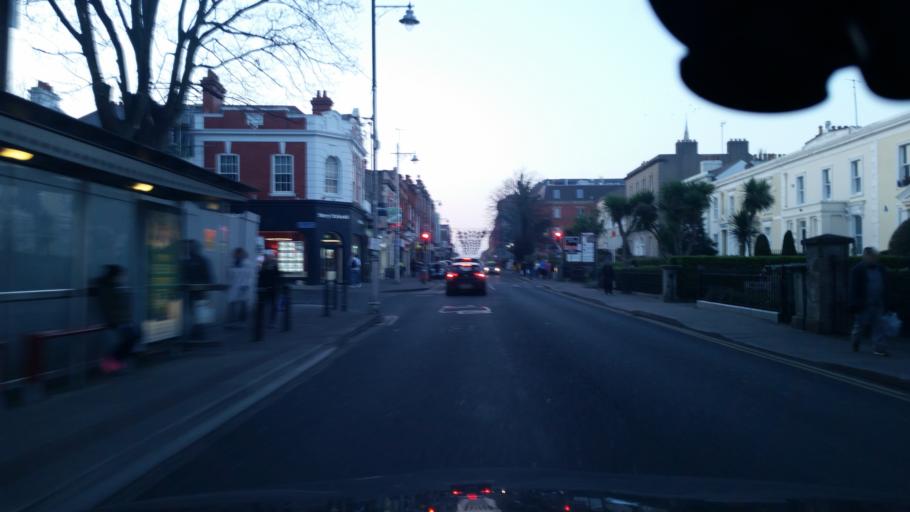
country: IE
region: Leinster
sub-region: Dun Laoghaire-Rathdown
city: Dun Laoghaire
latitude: 53.2908
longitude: -6.1326
